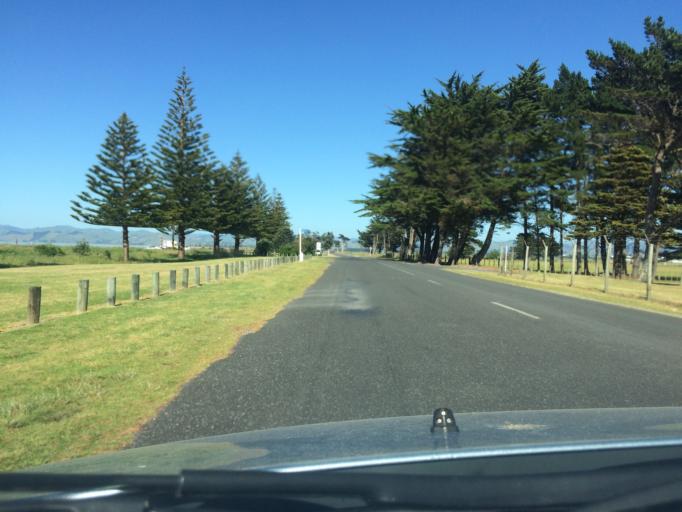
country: NZ
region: Gisborne
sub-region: Gisborne District
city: Gisborne
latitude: -38.6728
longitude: 177.9936
